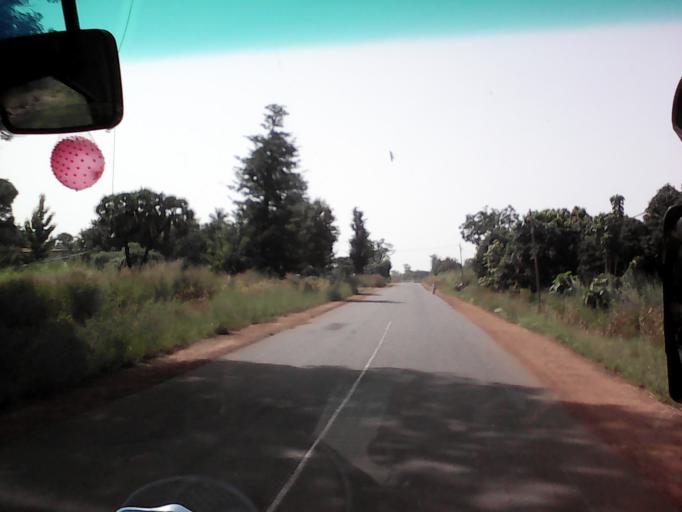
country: TG
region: Centrale
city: Sotouboua
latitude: 8.6943
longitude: 1.0237
